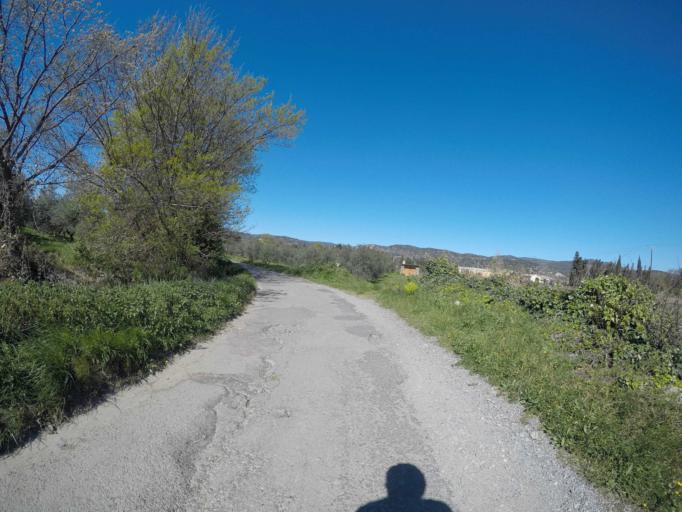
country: FR
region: Languedoc-Roussillon
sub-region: Departement des Pyrenees-Orientales
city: Ille-sur-Tet
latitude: 42.6823
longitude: 2.6464
